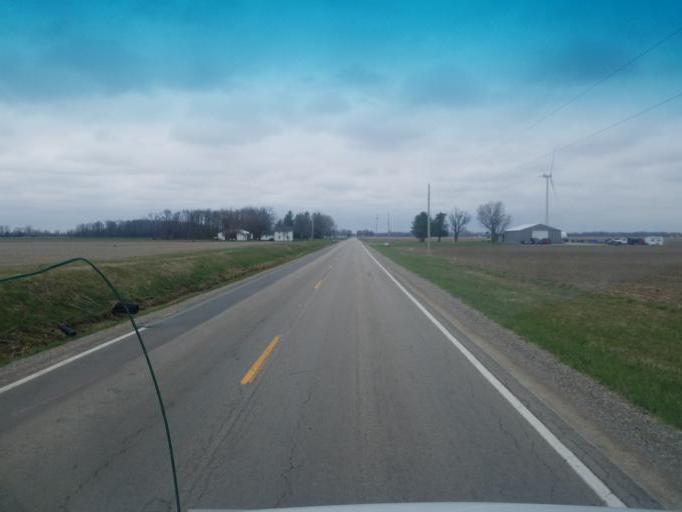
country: US
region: Ohio
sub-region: Paulding County
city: Payne
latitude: 41.0513
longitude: -84.7267
